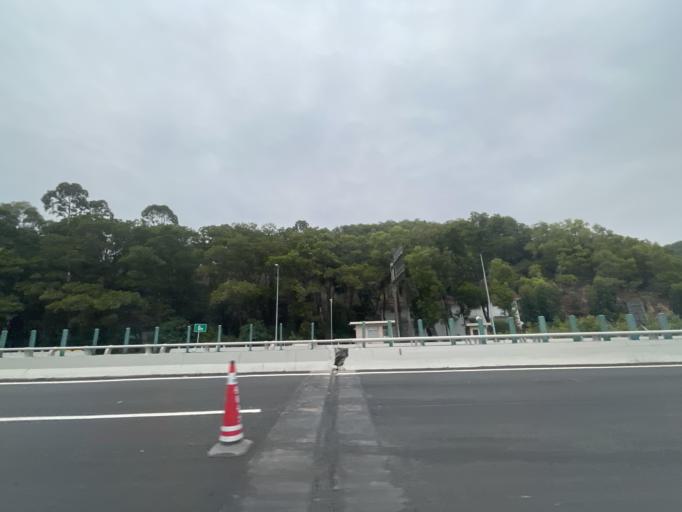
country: CN
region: Guangdong
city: Xinwan
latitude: 22.8009
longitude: 113.6222
